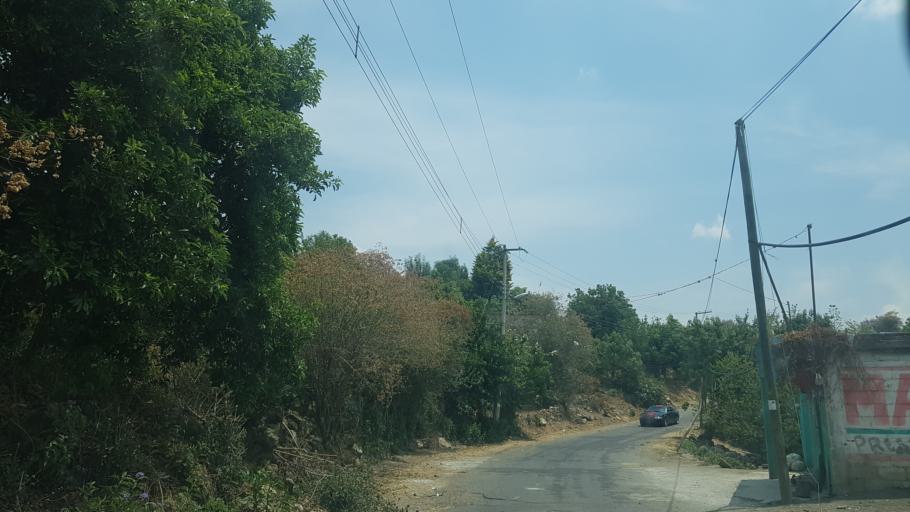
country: MX
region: Puebla
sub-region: Tochimilco
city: La Magdalena Yancuitlalpan
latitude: 18.8874
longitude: -98.6062
